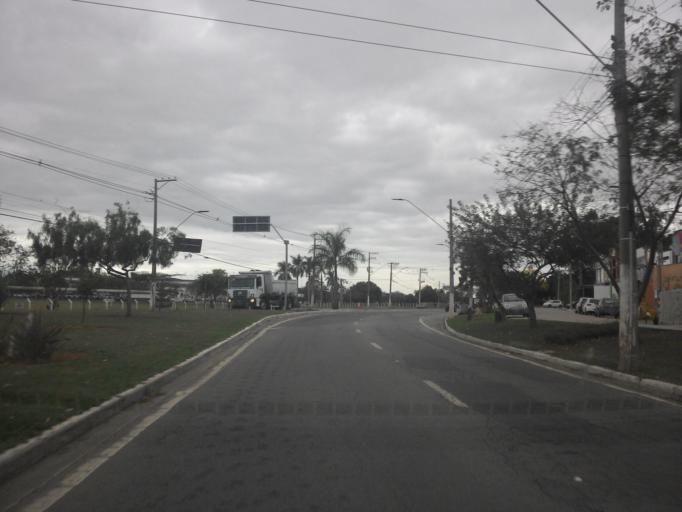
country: BR
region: Sao Paulo
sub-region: Taubate
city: Taubate
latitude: -23.0252
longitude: -45.5928
